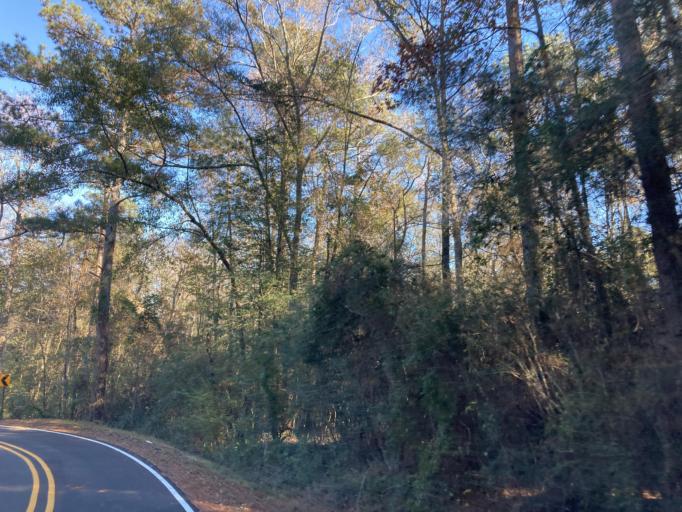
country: US
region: Mississippi
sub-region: Lamar County
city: Sumrall
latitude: 31.3538
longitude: -89.5698
